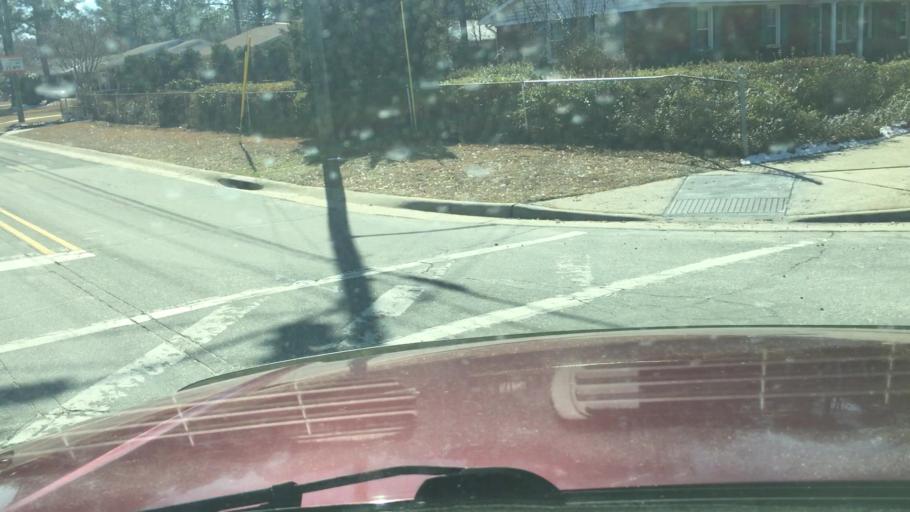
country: US
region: North Carolina
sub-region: Cumberland County
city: Hope Mills
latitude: 35.0277
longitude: -78.9383
